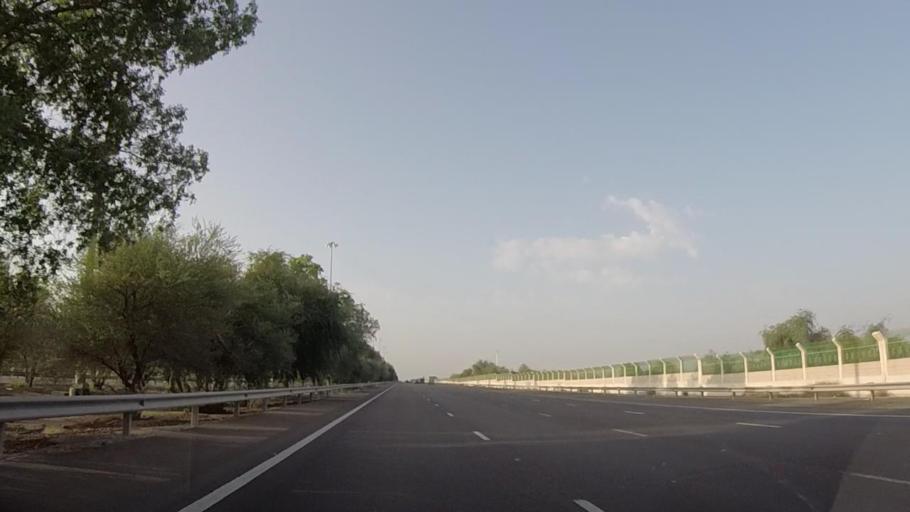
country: AE
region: Dubai
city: Dubai
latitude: 24.7606
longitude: 54.8423
